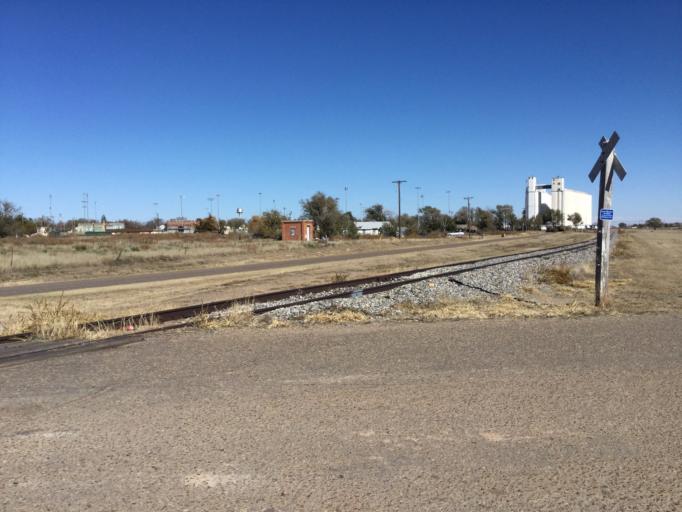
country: US
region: Kansas
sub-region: Morton County
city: Elkhart
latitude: 36.9936
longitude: -101.9006
